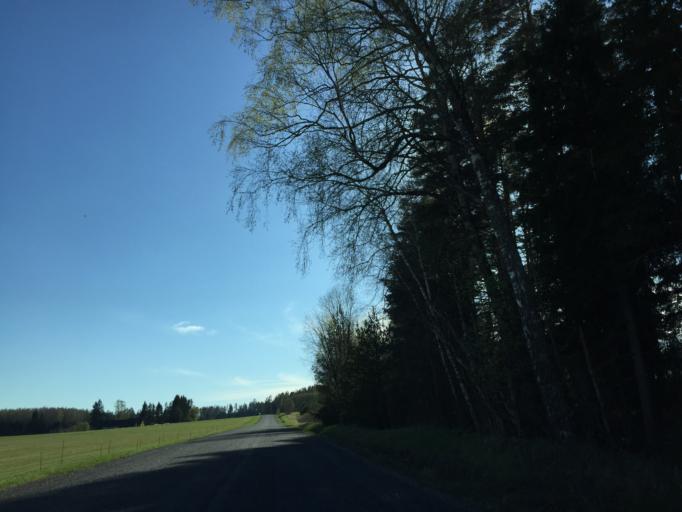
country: EE
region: Valgamaa
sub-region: Valga linn
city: Valga
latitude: 57.8281
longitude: 26.2181
